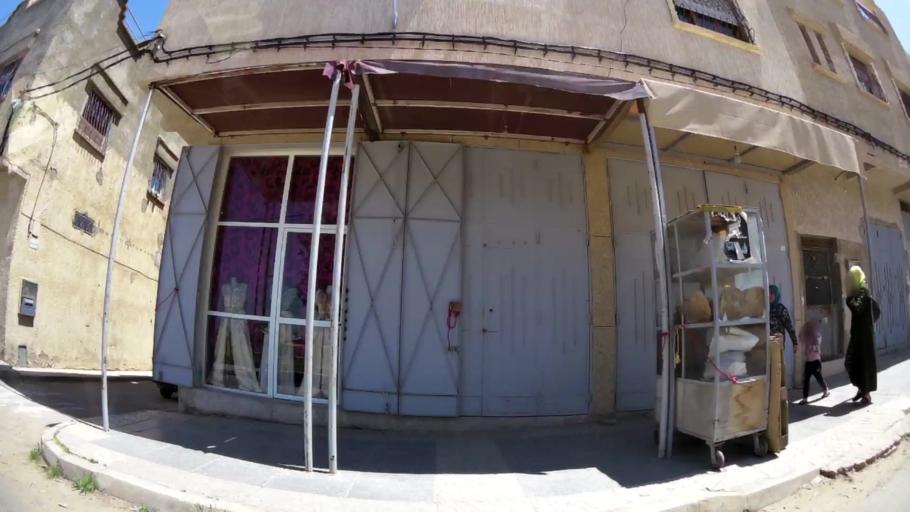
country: MA
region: Oriental
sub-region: Oujda-Angad
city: Oujda
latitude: 34.6870
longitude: -1.9532
